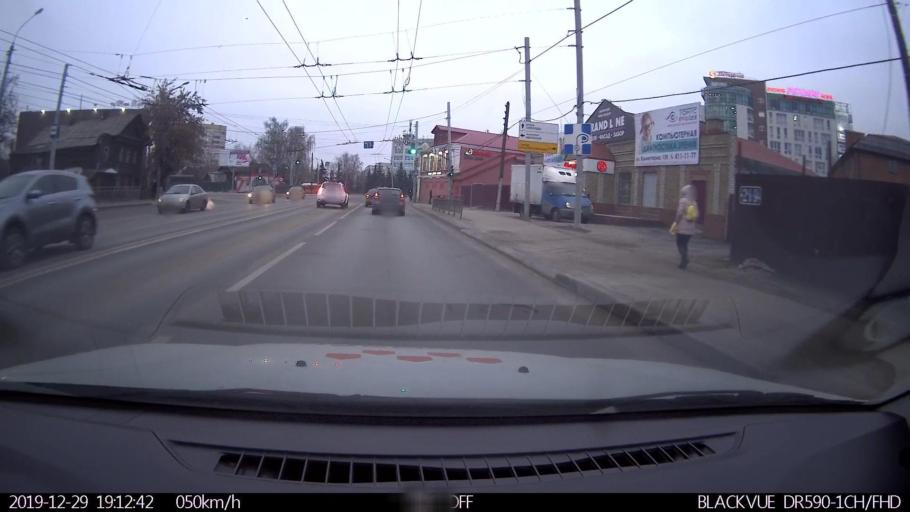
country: RU
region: Nizjnij Novgorod
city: Neklyudovo
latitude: 56.3606
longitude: 43.8627
